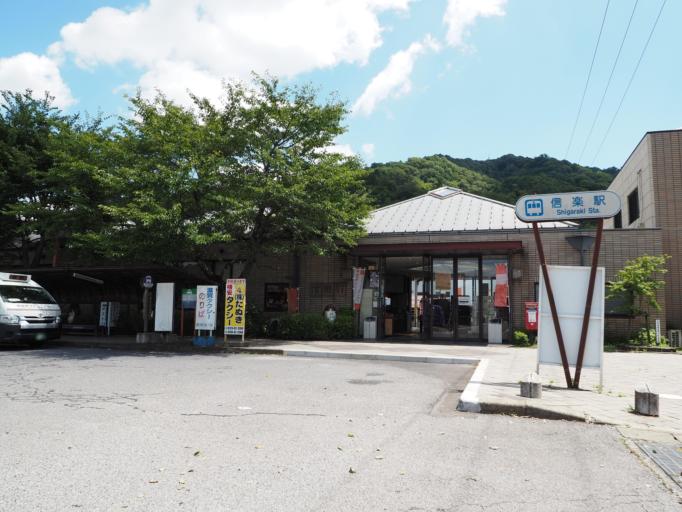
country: JP
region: Mie
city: Ueno-ebisumachi
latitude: 34.8769
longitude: 136.0607
